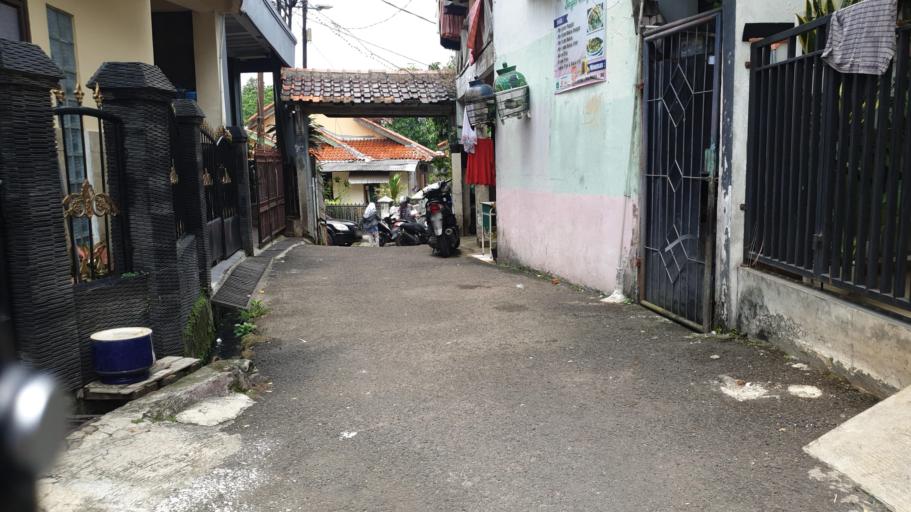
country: ID
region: West Java
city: Pamulang
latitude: -6.3025
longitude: 106.7794
